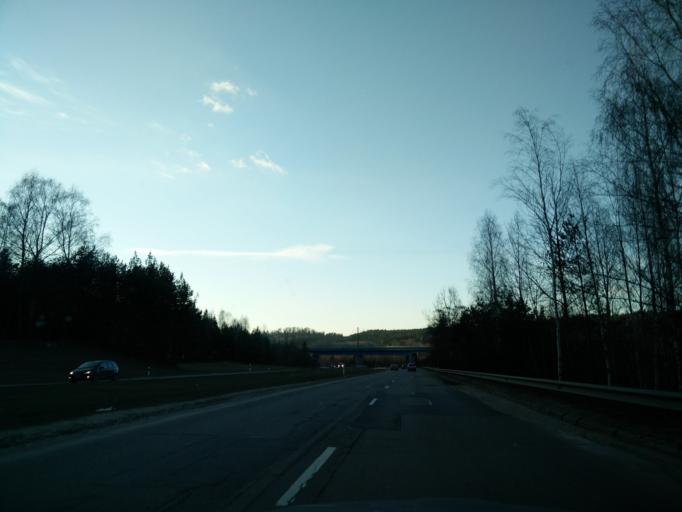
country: LT
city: Skaidiskes
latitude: 54.6912
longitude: 25.3926
